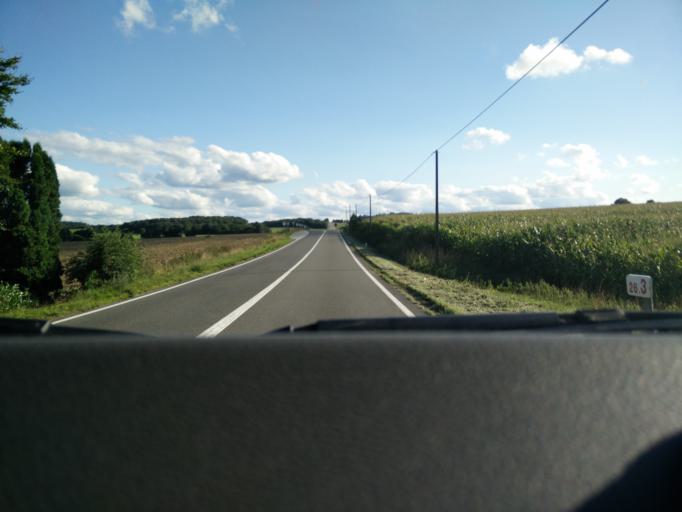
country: BE
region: Wallonia
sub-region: Province du Hainaut
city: Beaumont
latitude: 50.2232
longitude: 4.2279
